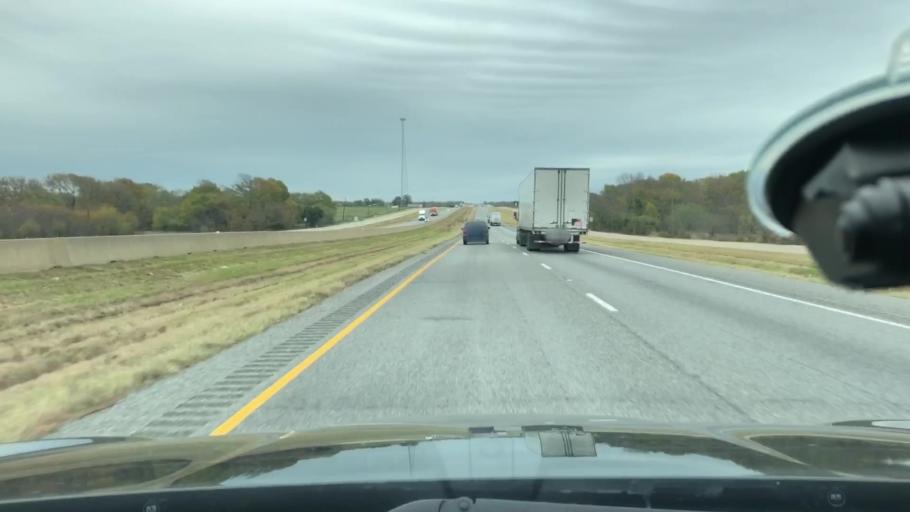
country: US
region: Texas
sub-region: Hunt County
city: Commerce
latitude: 33.1299
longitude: -95.8827
